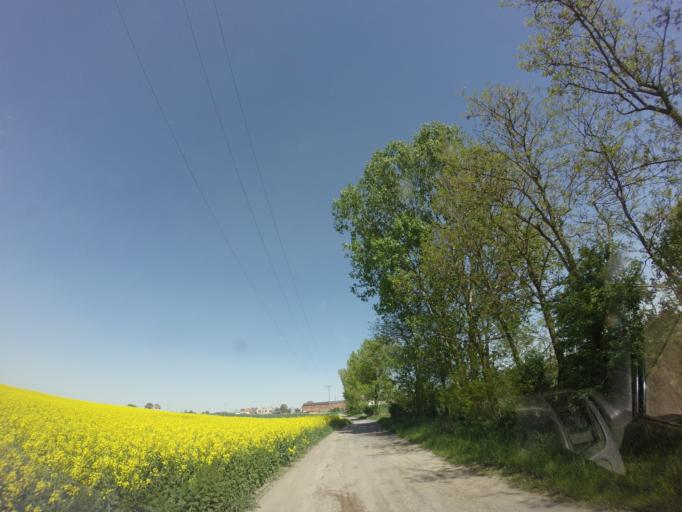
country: PL
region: West Pomeranian Voivodeship
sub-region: Powiat choszczenski
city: Pelczyce
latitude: 53.0224
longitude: 15.3591
